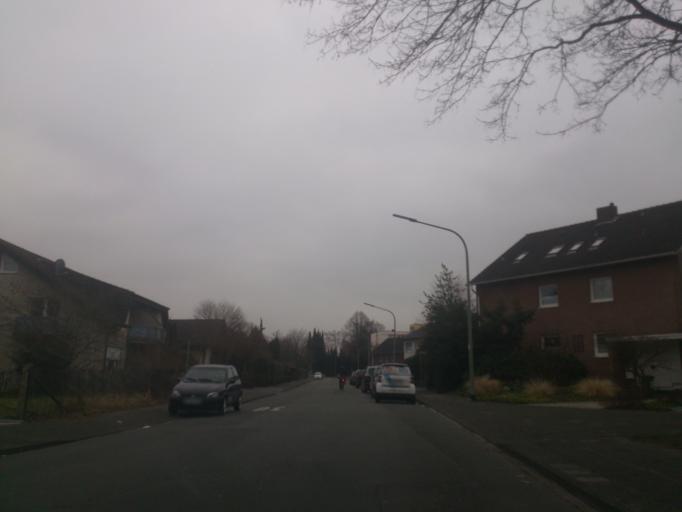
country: DE
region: North Rhine-Westphalia
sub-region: Regierungsbezirk Detmold
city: Paderborn
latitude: 51.7301
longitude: 8.7706
